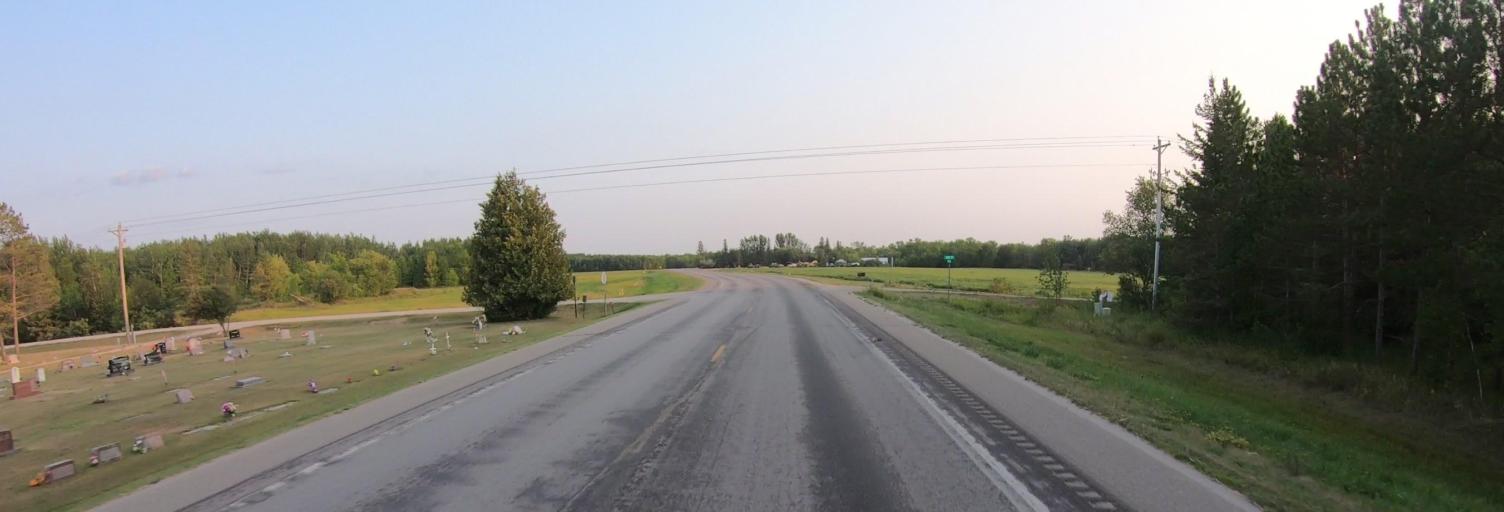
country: US
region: Minnesota
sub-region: Roseau County
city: Warroad
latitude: 48.8875
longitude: -95.3202
